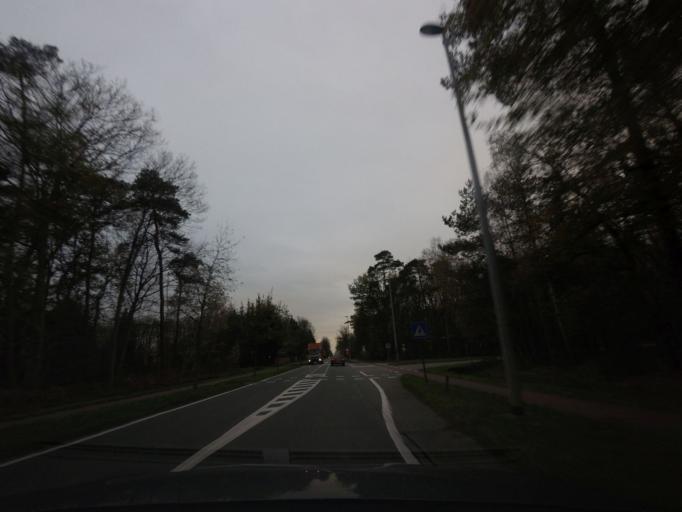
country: BE
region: Flanders
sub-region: Provincie Antwerpen
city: Brecht
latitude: 51.3293
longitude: 4.6045
